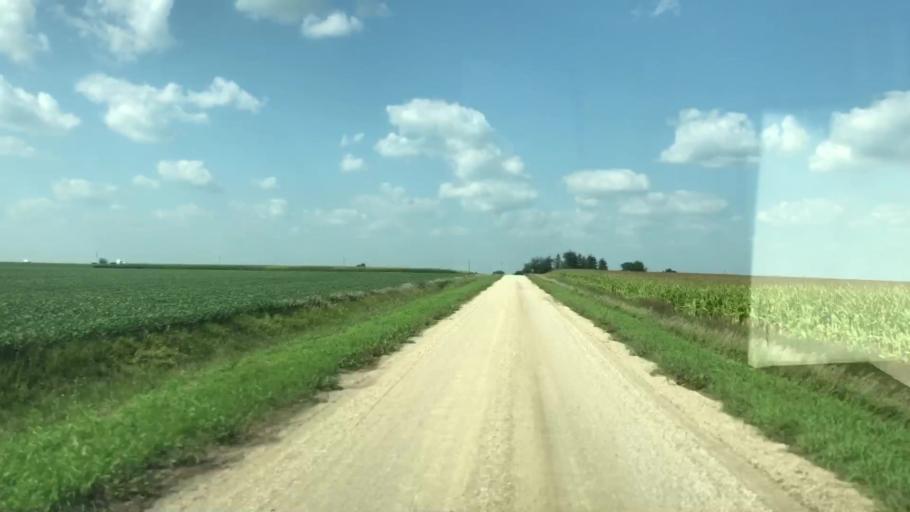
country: US
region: Iowa
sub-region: O'Brien County
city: Sheldon
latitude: 43.1813
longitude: -95.7824
